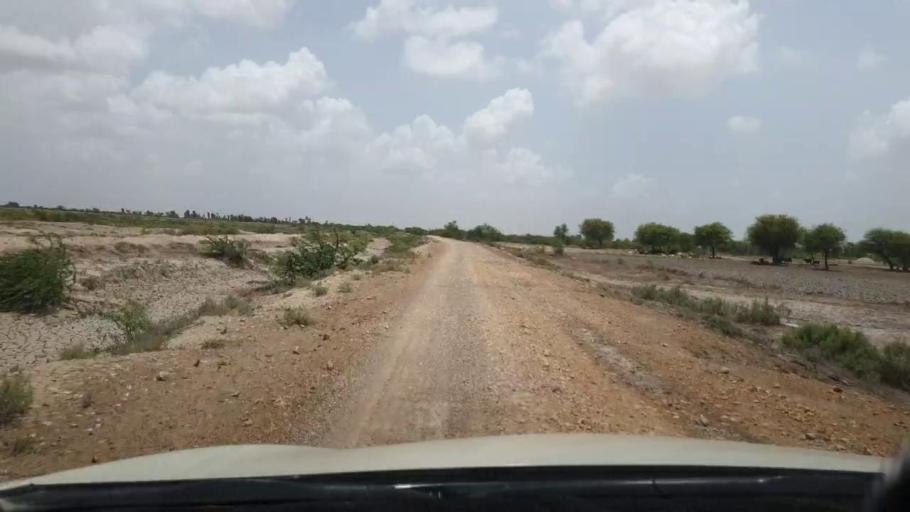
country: PK
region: Sindh
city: Kadhan
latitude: 24.3659
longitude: 68.9269
